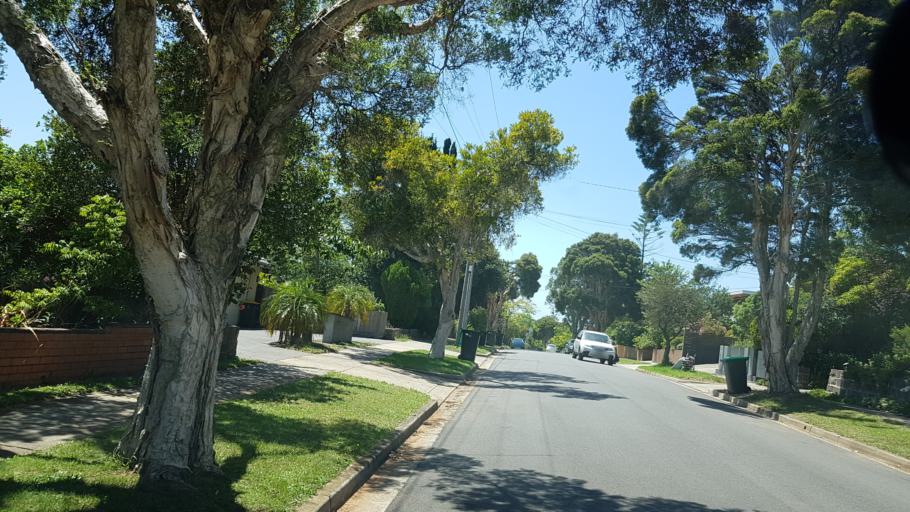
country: AU
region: Victoria
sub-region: Manningham
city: Templestowe Lower
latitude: -37.7614
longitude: 145.1020
